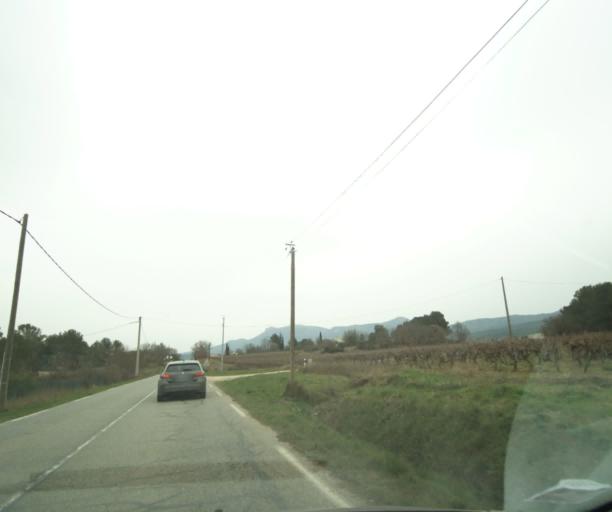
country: FR
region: Provence-Alpes-Cote d'Azur
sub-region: Departement des Bouches-du-Rhone
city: Trets
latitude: 43.4492
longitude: 5.6671
